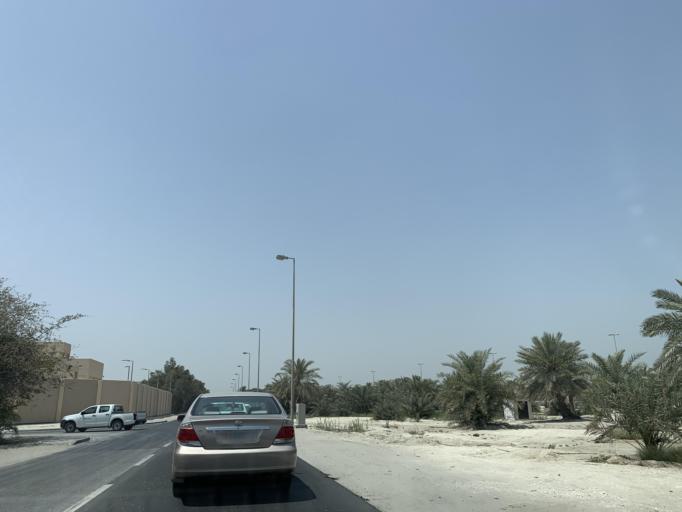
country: BH
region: Manama
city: Jidd Hafs
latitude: 26.1966
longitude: 50.5504
